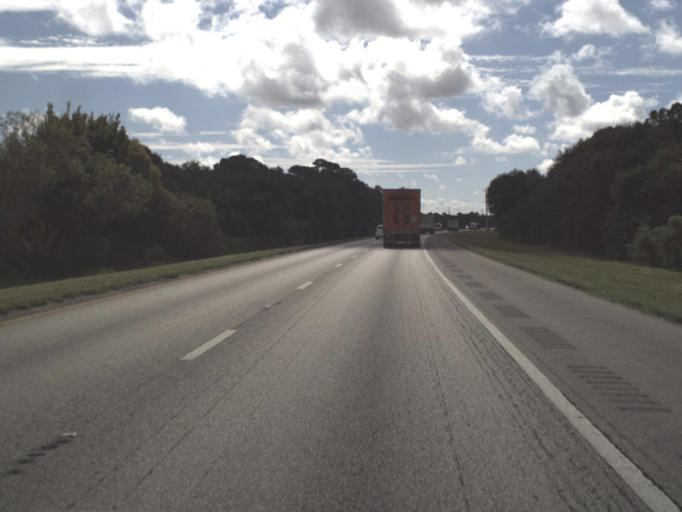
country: US
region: Florida
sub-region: Sarasota County
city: North Port
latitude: 27.0951
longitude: -82.1260
